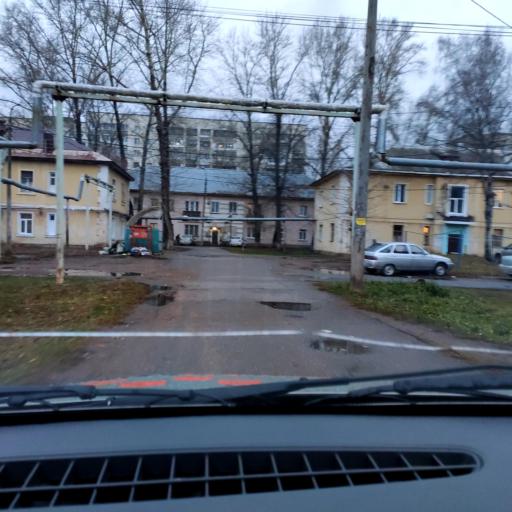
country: RU
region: Bashkortostan
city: Avdon
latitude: 54.6968
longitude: 55.8278
